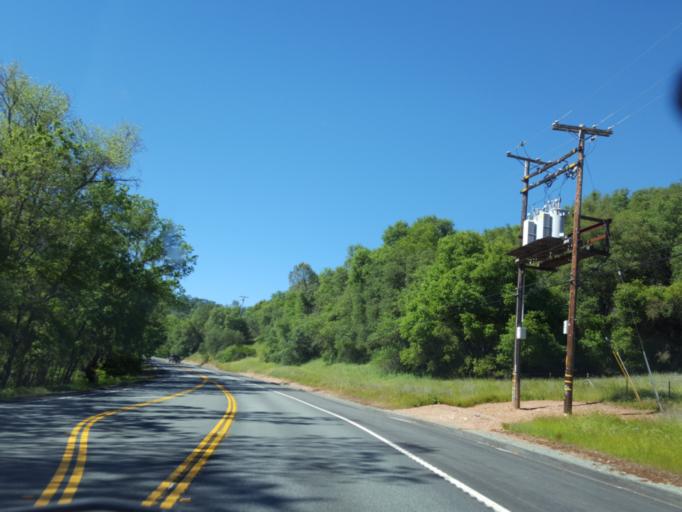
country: US
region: California
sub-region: Calaveras County
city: San Andreas
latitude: 38.2382
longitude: -120.7107
